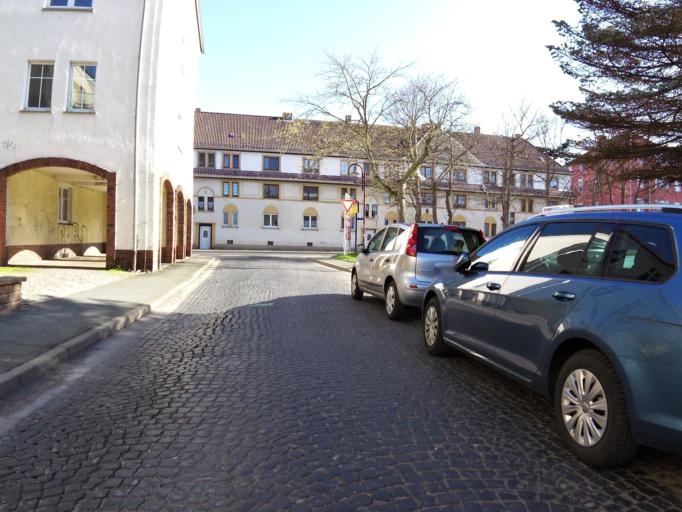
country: DE
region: Thuringia
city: Gotha
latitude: 50.9369
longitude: 10.7054
